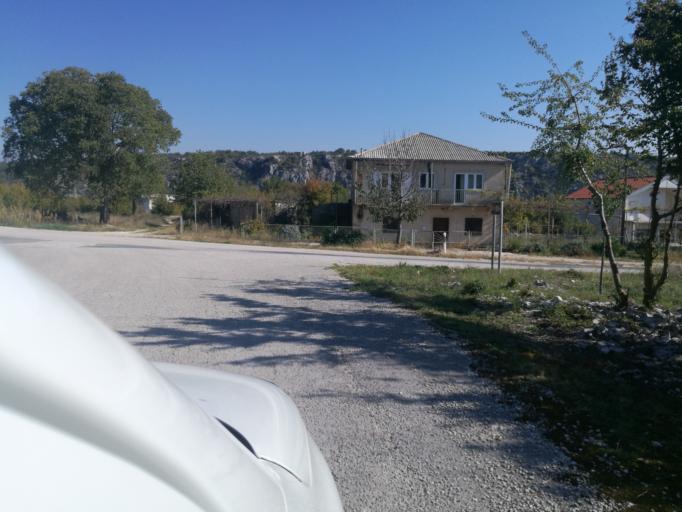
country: HR
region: Splitsko-Dalmatinska
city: Trilj
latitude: 43.5431
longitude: 16.7330
